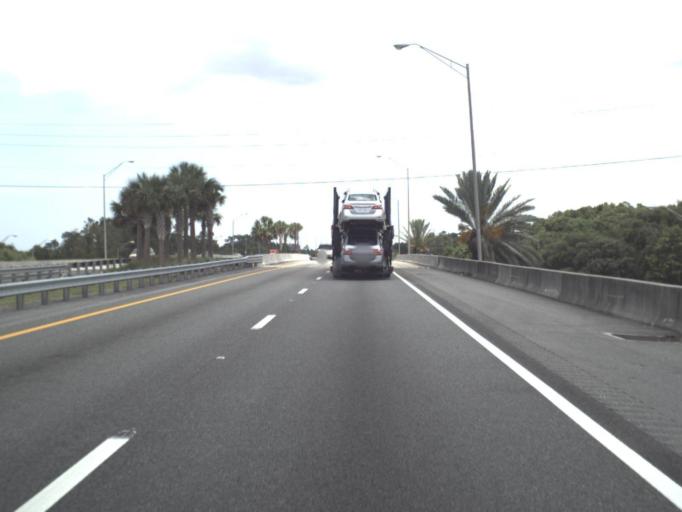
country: US
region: Florida
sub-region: Duval County
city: Jacksonville
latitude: 30.3249
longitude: -81.5279
